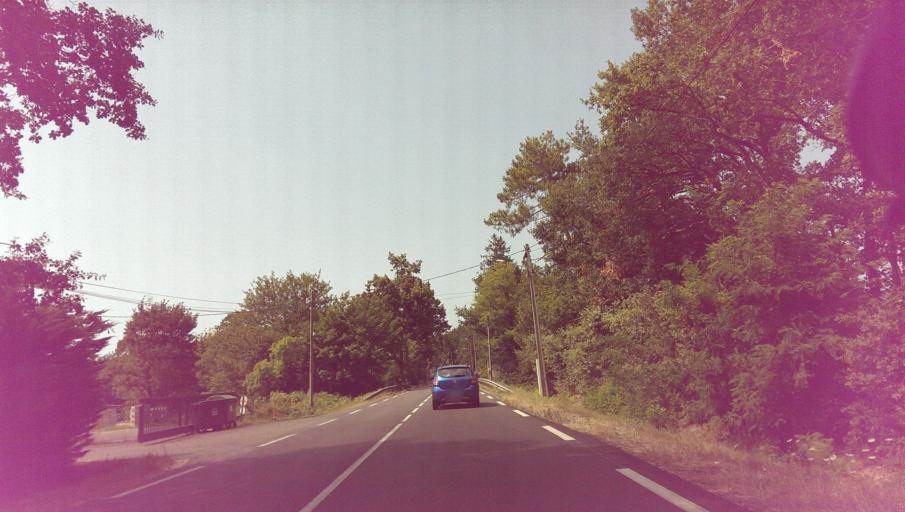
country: FR
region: Aquitaine
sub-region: Departement des Landes
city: Sabres
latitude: 44.1435
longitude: -0.7295
